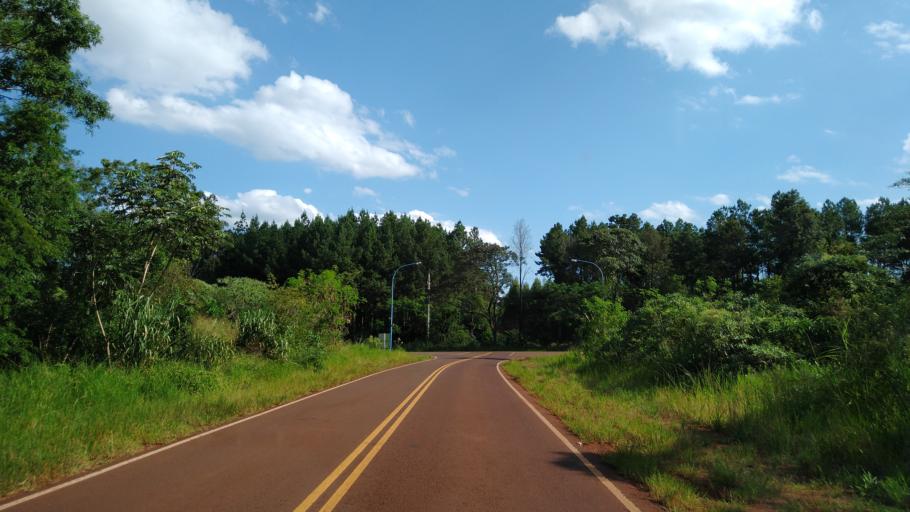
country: AR
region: Misiones
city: Puerto Piray
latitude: -26.4905
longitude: -54.6761
